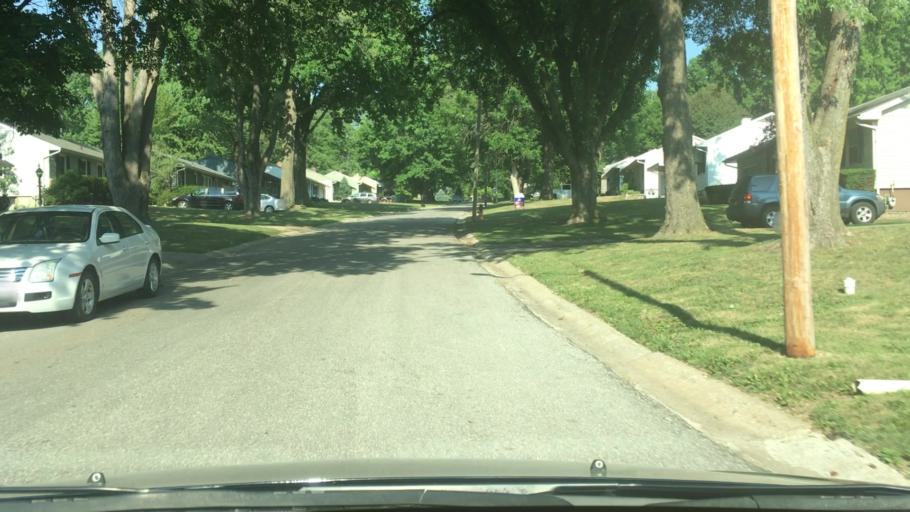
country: US
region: Kansas
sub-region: Johnson County
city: Leawood
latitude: 38.9654
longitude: -94.5975
